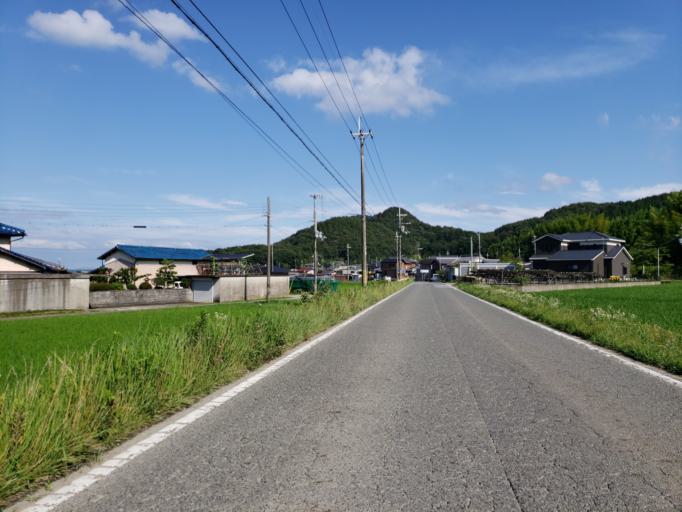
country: JP
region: Hyogo
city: Himeji
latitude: 34.8973
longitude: 134.8005
